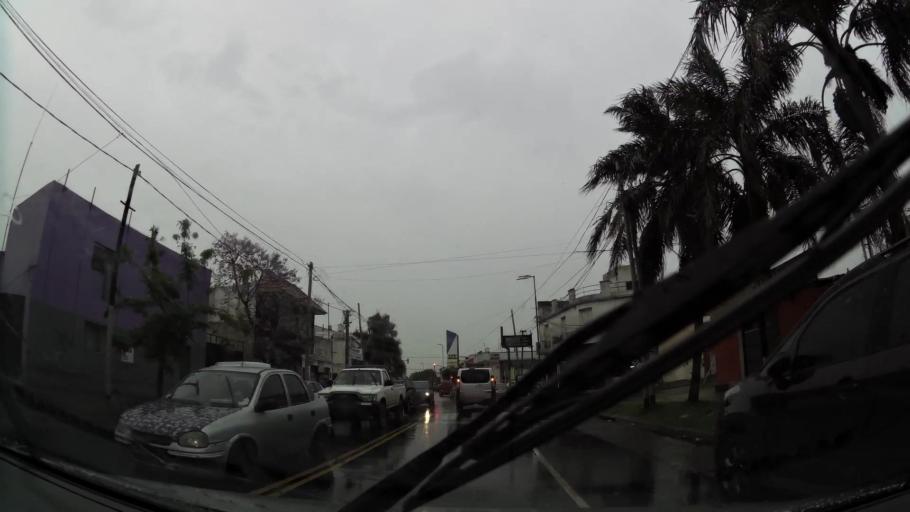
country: AR
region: Buenos Aires
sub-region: Partido de Lanus
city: Lanus
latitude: -34.7059
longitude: -58.4045
